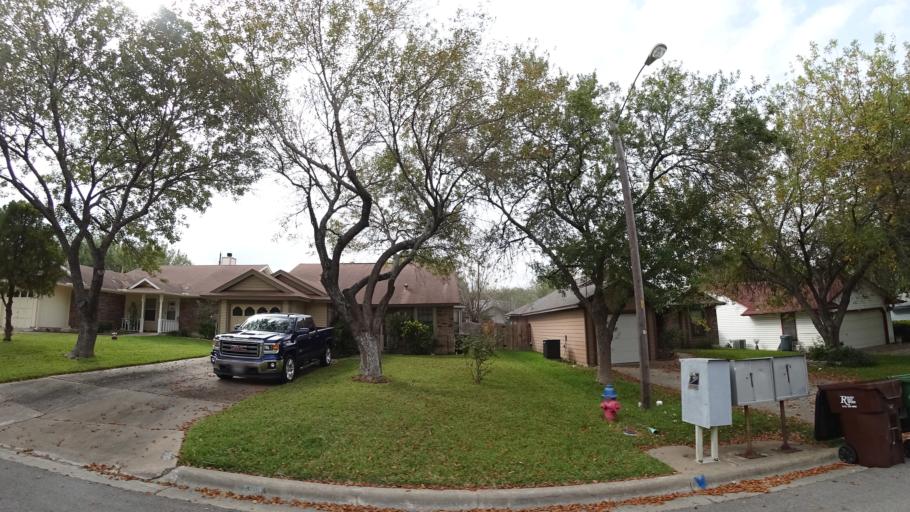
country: US
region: Texas
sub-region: Williamson County
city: Round Rock
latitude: 30.4888
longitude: -97.6874
